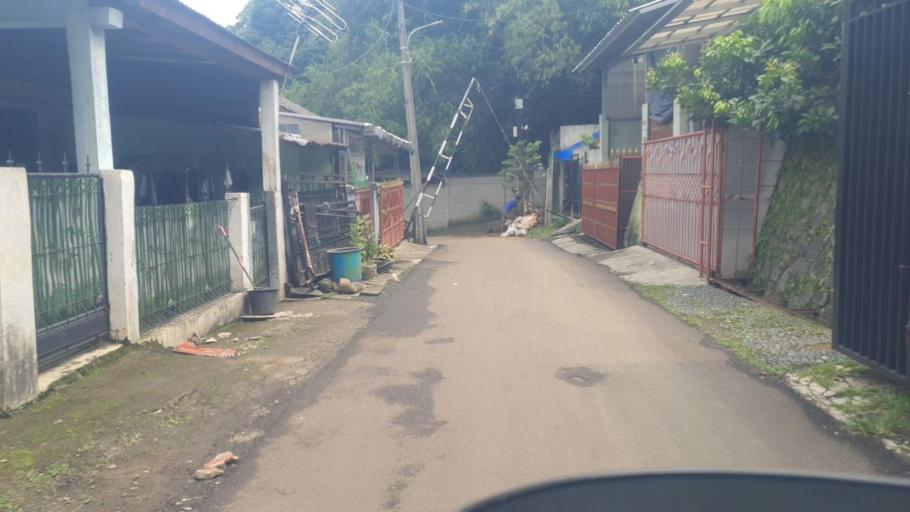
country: ID
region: West Java
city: Bogor
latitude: -6.5837
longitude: 106.7849
